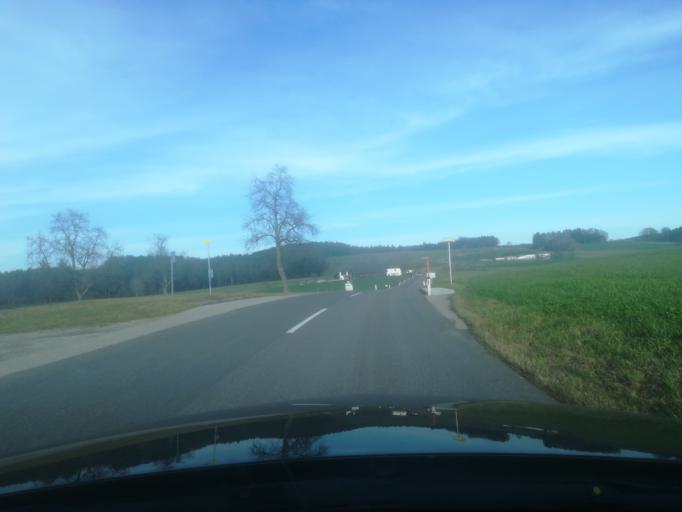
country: AT
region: Upper Austria
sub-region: Politischer Bezirk Perg
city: Perg
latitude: 48.3190
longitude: 14.6637
